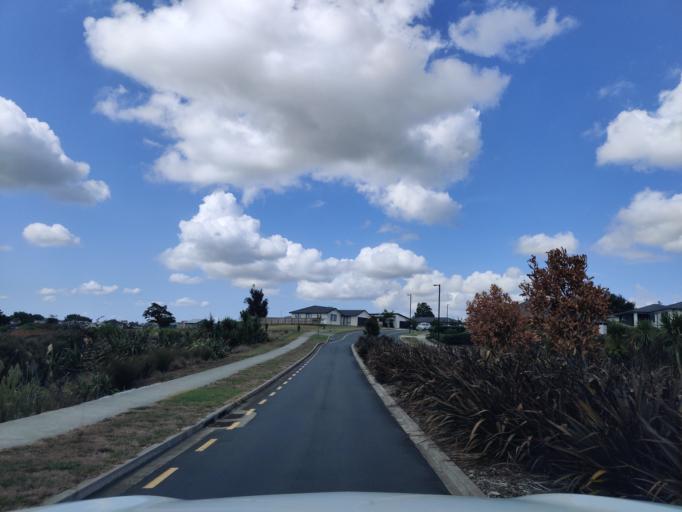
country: NZ
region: Auckland
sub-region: Auckland
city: Pukekohe East
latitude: -37.2406
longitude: 175.0161
